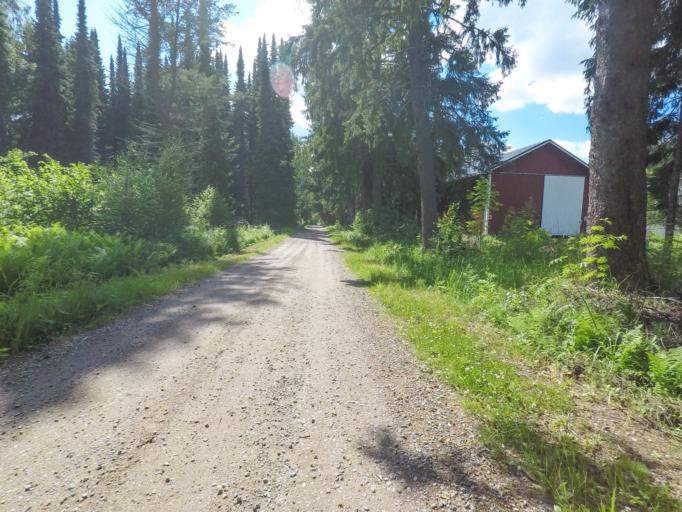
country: FI
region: Southern Savonia
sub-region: Savonlinna
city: Punkaharju
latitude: 61.8045
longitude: 29.3195
